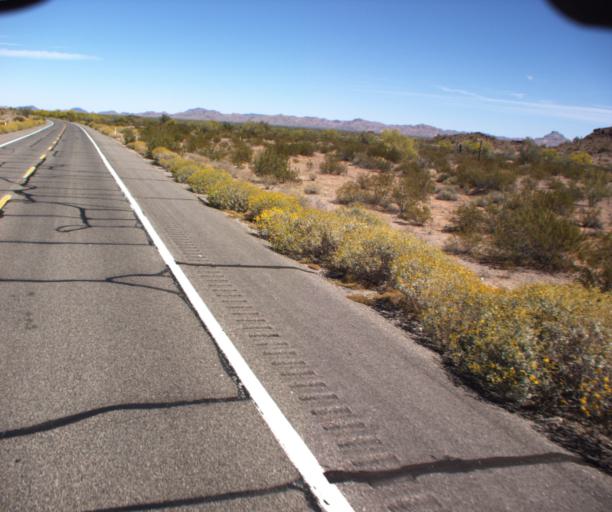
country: US
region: Arizona
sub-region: Pima County
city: Ajo
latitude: 32.5640
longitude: -112.8771
